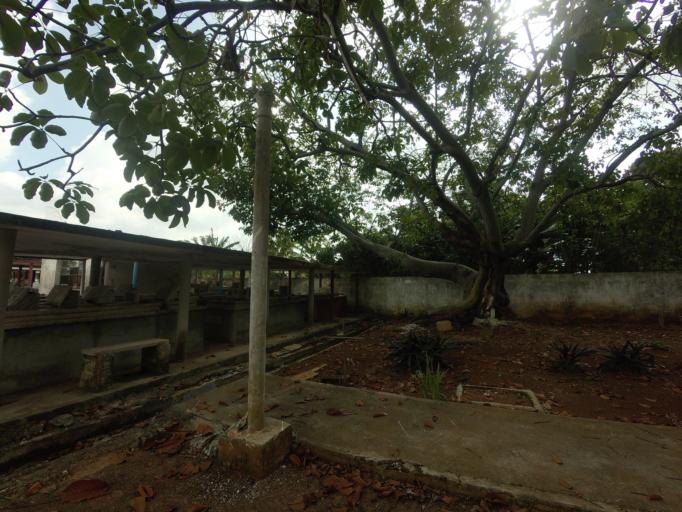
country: CU
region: Artemisa
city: Bauta
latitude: 22.9822
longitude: -82.5520
